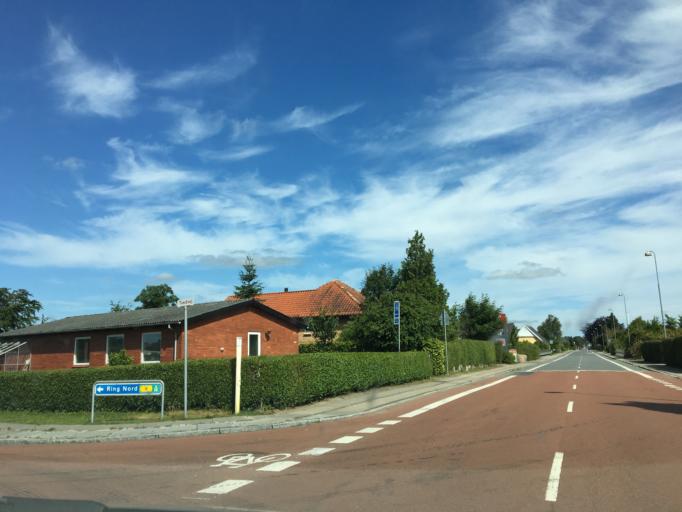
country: DK
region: South Denmark
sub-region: Svendborg Kommune
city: Svendborg
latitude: 55.0784
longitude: 10.6245
